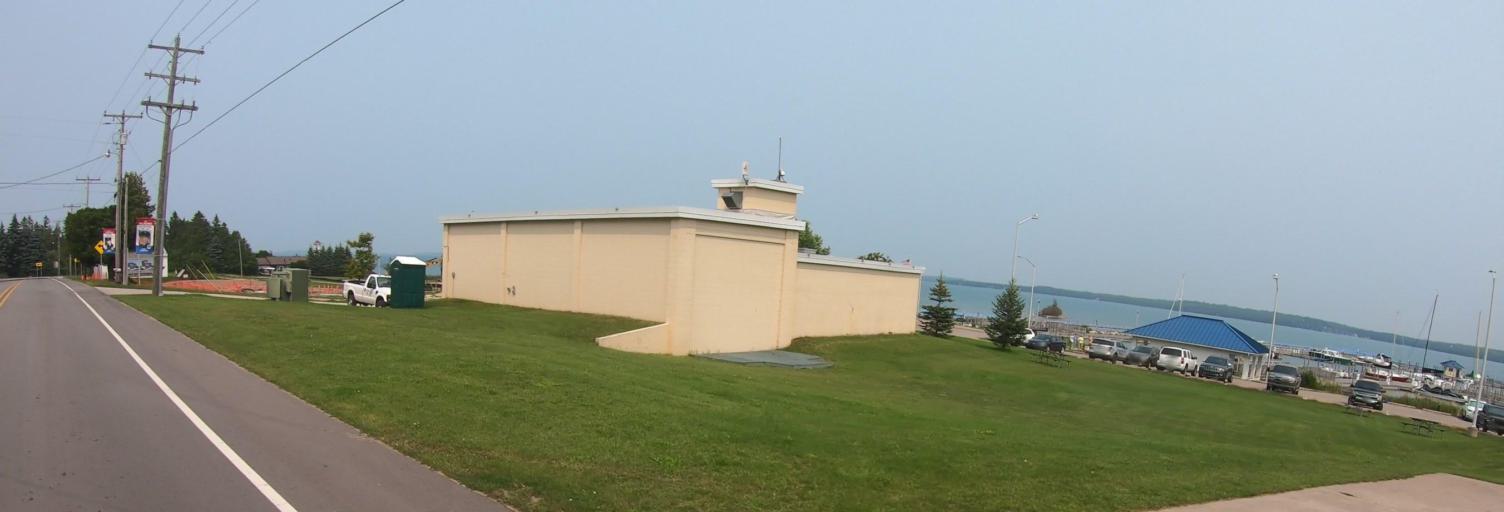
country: CA
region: Ontario
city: Thessalon
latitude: 45.9981
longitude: -83.9018
